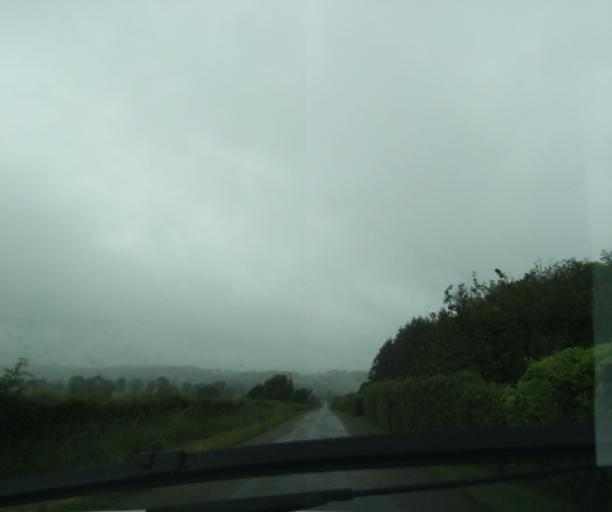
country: FR
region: Bourgogne
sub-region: Departement de Saone-et-Loire
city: Charolles
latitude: 46.4164
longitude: 4.2670
